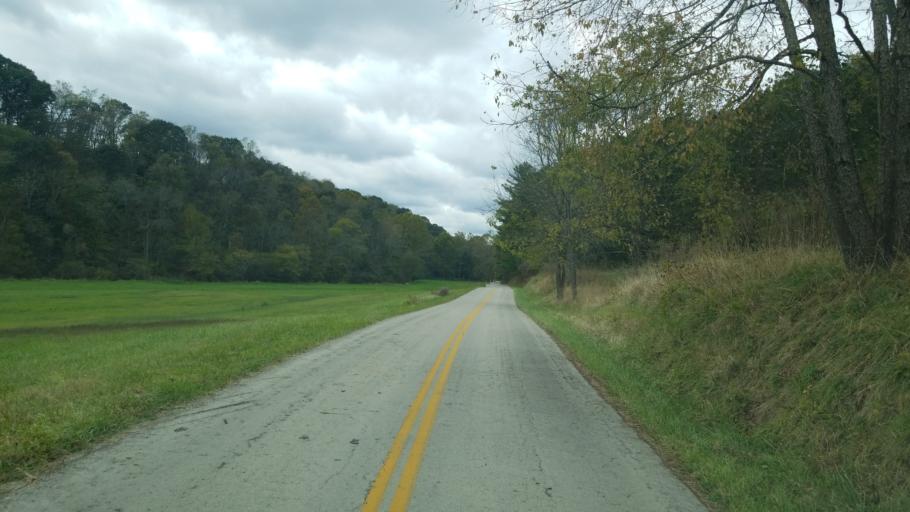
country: US
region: Ohio
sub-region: Jackson County
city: Wellston
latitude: 39.1649
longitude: -82.6306
